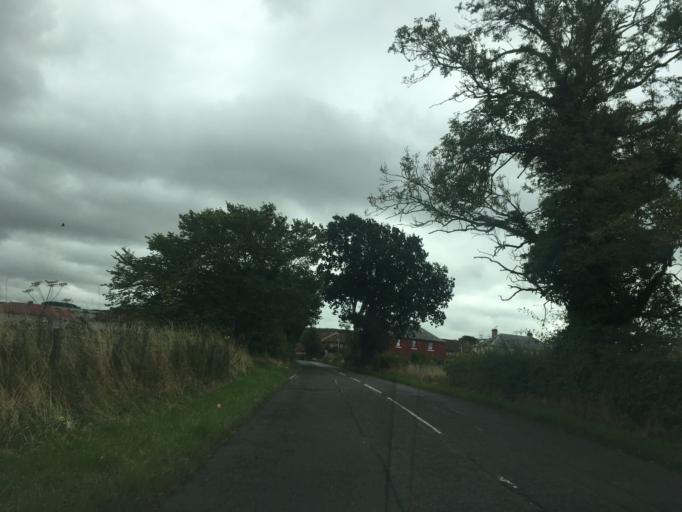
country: GB
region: Scotland
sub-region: Midlothian
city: Dalkeith
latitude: 55.8743
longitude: -3.0634
